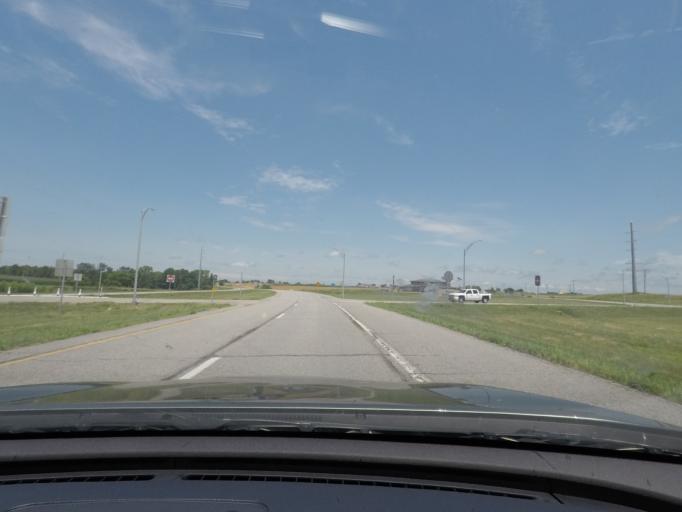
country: US
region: Missouri
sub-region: Saline County
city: Marshall
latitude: 39.0792
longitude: -93.1965
